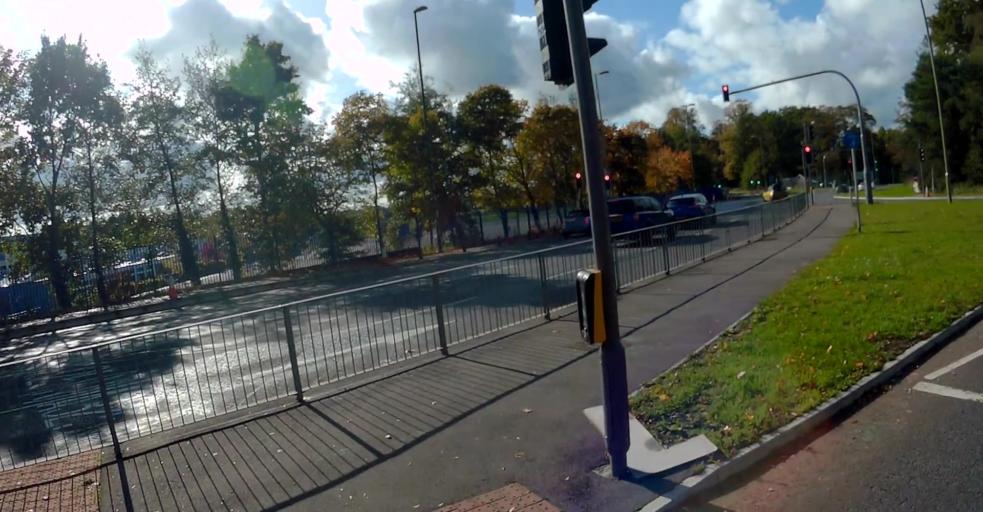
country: GB
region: England
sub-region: Hampshire
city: Farnborough
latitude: 51.2734
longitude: -0.7557
